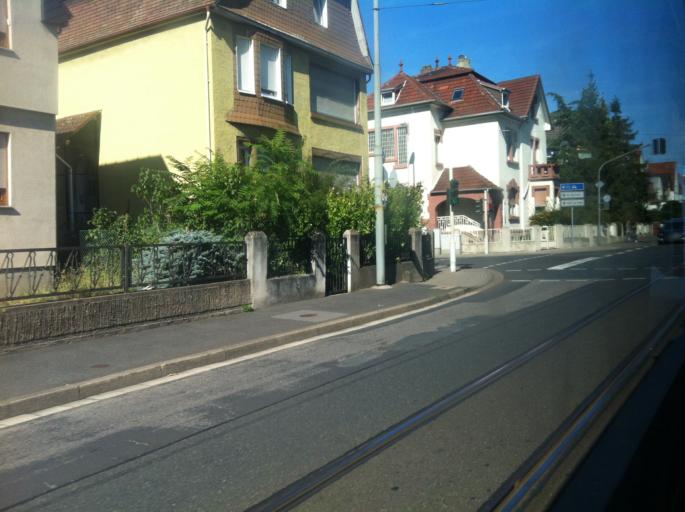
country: DE
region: Rheinland-Pfalz
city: Budenheim
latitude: 50.0042
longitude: 8.2157
